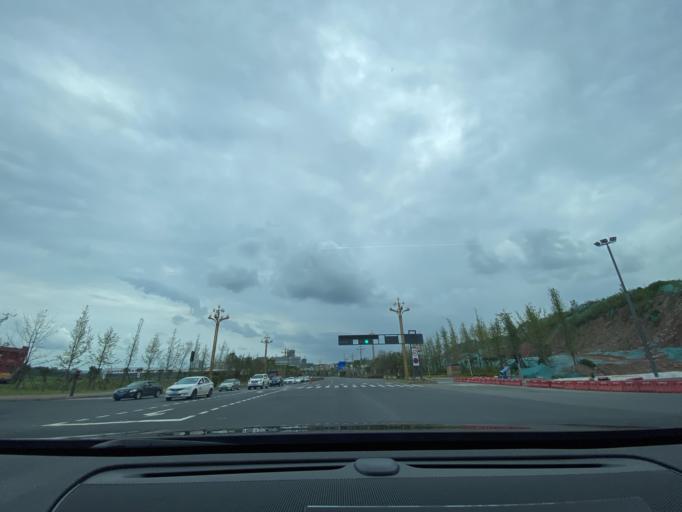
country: CN
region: Sichuan
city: Jiancheng
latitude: 30.4464
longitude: 104.4959
